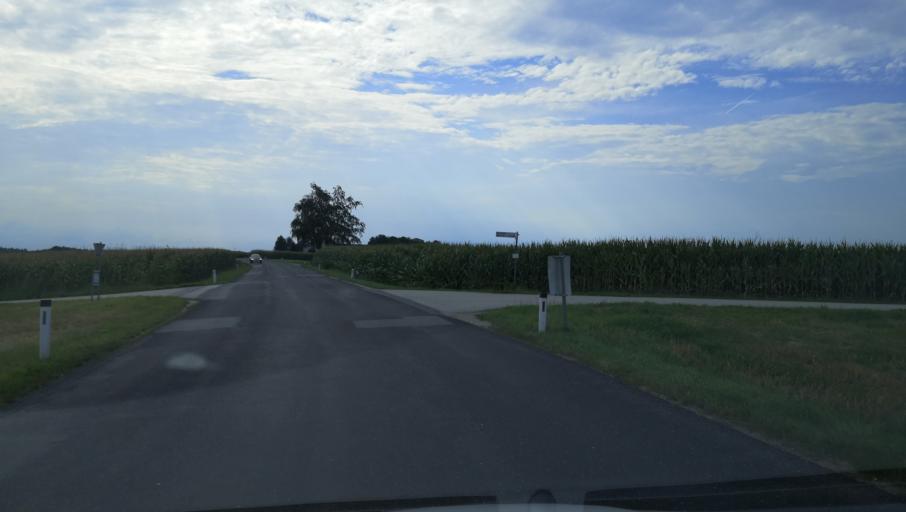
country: AT
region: Lower Austria
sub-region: Politischer Bezirk Amstetten
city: Amstetten
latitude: 48.1472
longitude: 14.8682
